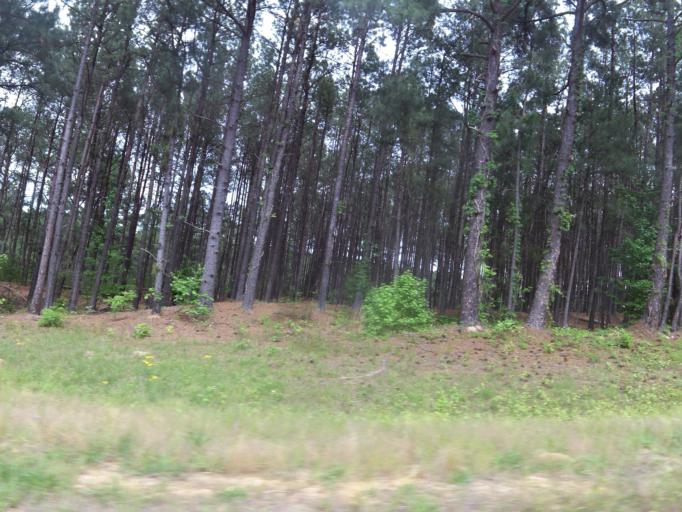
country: US
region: Georgia
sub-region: Jefferson County
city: Wrens
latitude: 33.3289
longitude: -82.4541
